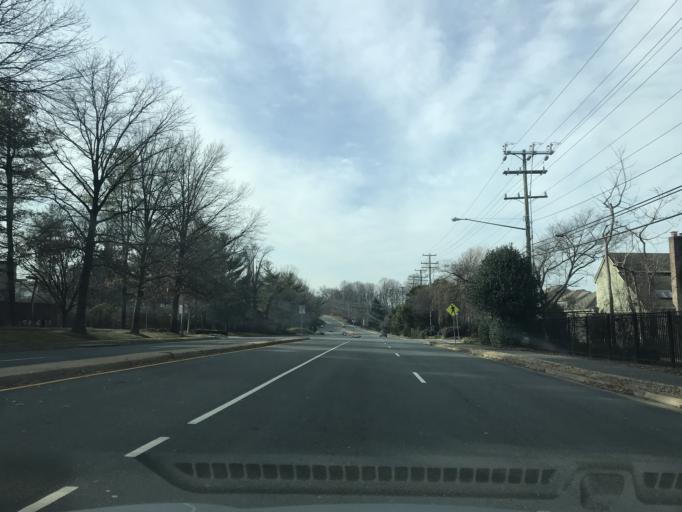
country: US
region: Virginia
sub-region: Fairfax County
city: Oakton
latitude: 38.8773
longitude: -77.3071
